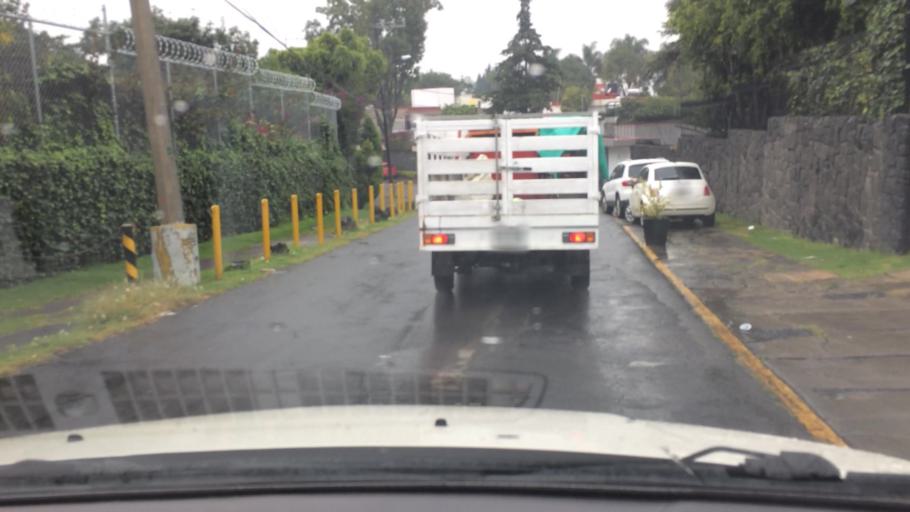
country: MX
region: Mexico City
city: Magdalena Contreras
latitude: 19.3302
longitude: -99.2003
